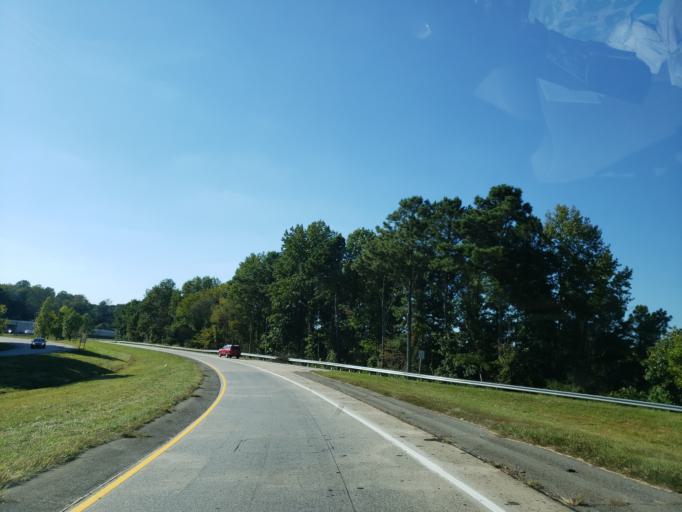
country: US
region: Georgia
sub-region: Cobb County
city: Marietta
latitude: 33.9868
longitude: -84.5409
